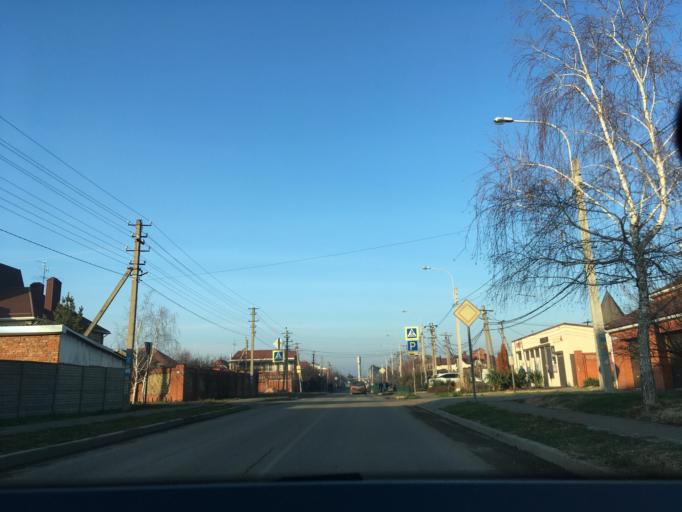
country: RU
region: Krasnodarskiy
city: Krasnodar
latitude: 45.1221
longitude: 39.0141
